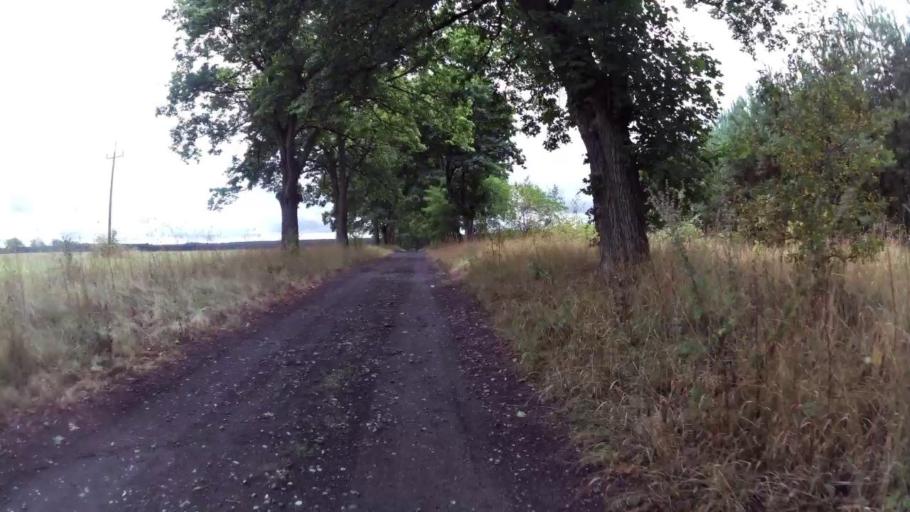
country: PL
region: West Pomeranian Voivodeship
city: Trzcinsko Zdroj
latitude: 52.8787
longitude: 14.7115
